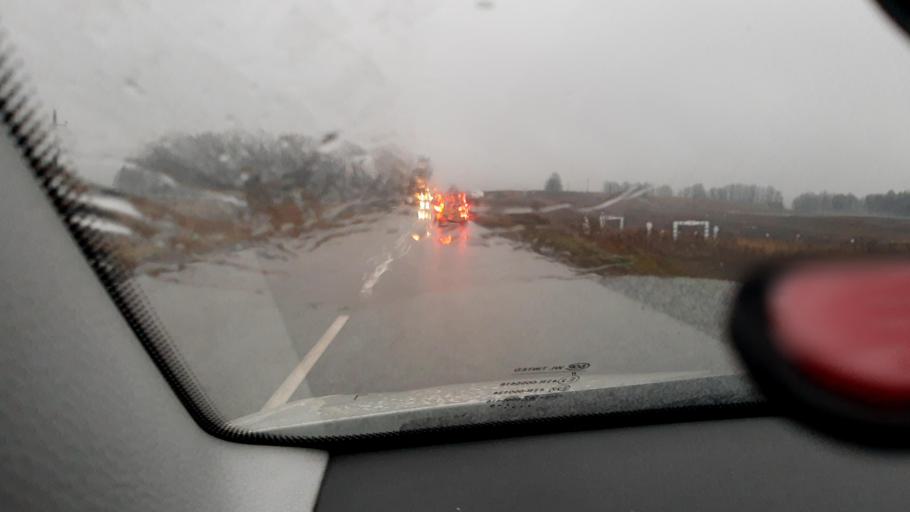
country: RU
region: Bashkortostan
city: Iglino
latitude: 54.9005
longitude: 56.1835
